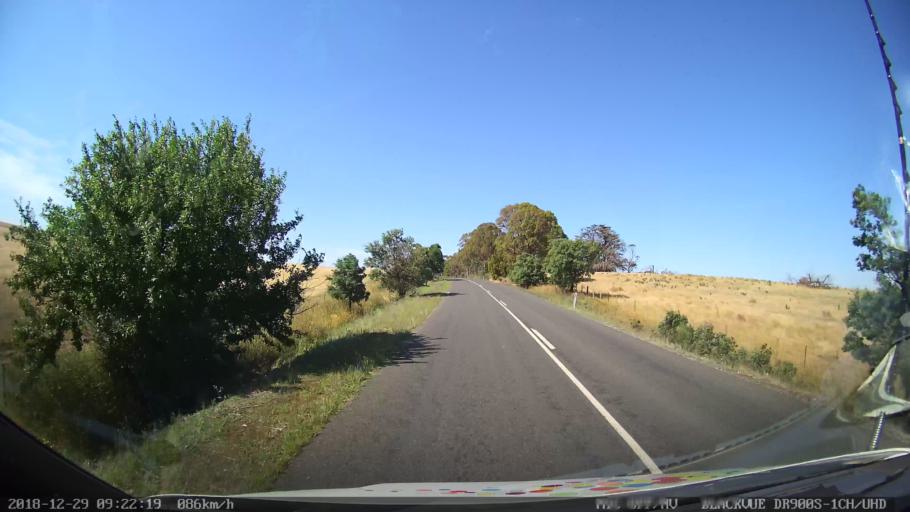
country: AU
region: New South Wales
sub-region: Upper Lachlan Shire
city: Crookwell
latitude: -34.5111
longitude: 149.4068
